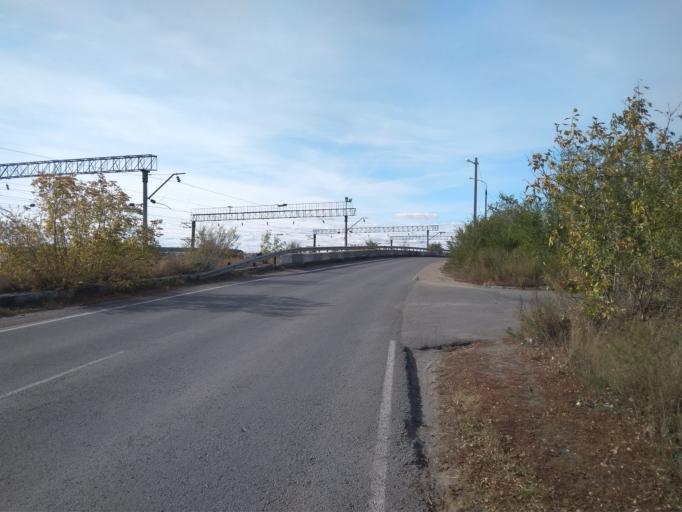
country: RU
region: Chelyabinsk
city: Troitsk
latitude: 54.0429
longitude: 61.6260
